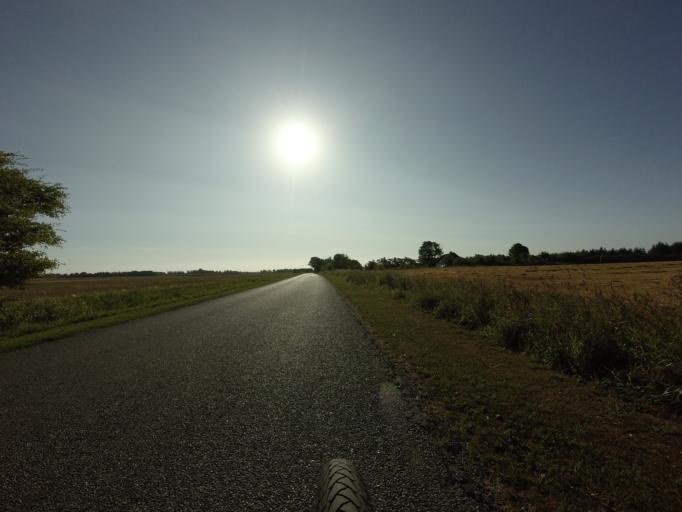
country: DK
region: North Denmark
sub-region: Hjorring Kommune
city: Vra
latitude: 57.3894
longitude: 9.9409
